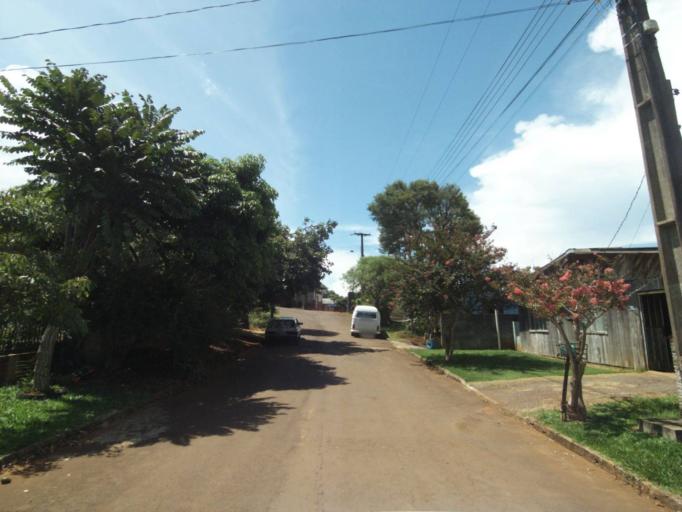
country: BR
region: Parana
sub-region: Guaraniacu
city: Guaraniacu
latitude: -25.0974
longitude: -52.8659
